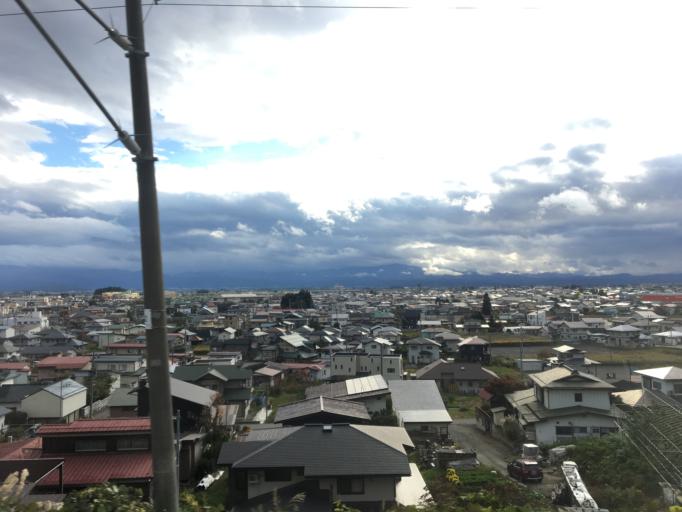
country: JP
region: Yamagata
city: Takahata
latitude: 38.0543
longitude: 140.1625
